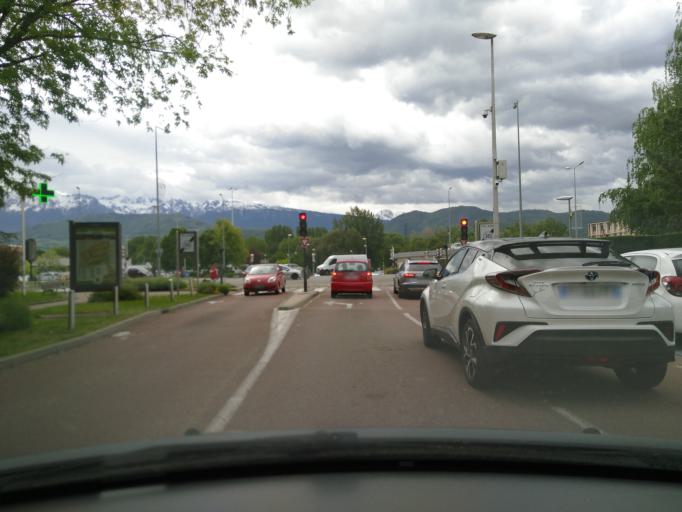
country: FR
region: Rhone-Alpes
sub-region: Departement de l'Isere
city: Corenc
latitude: 45.2033
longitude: 5.7609
